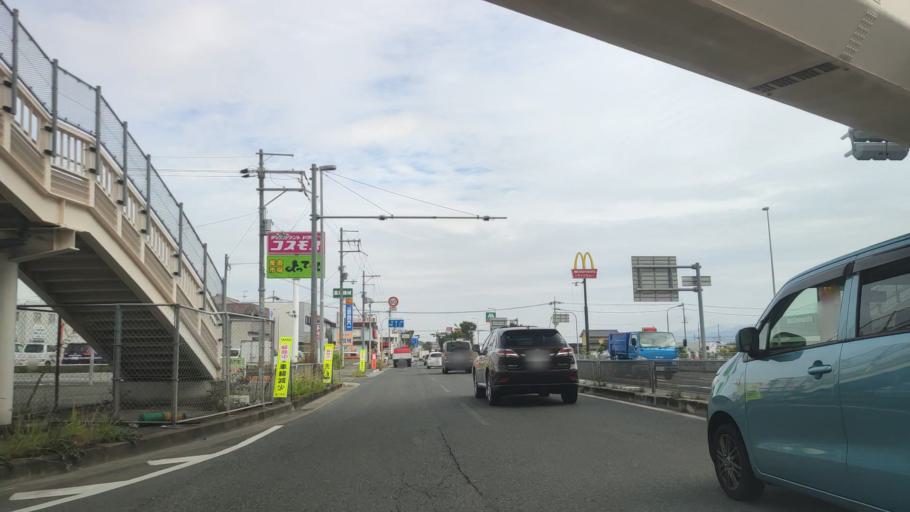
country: JP
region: Osaka
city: Tondabayashicho
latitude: 34.5341
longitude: 135.6047
